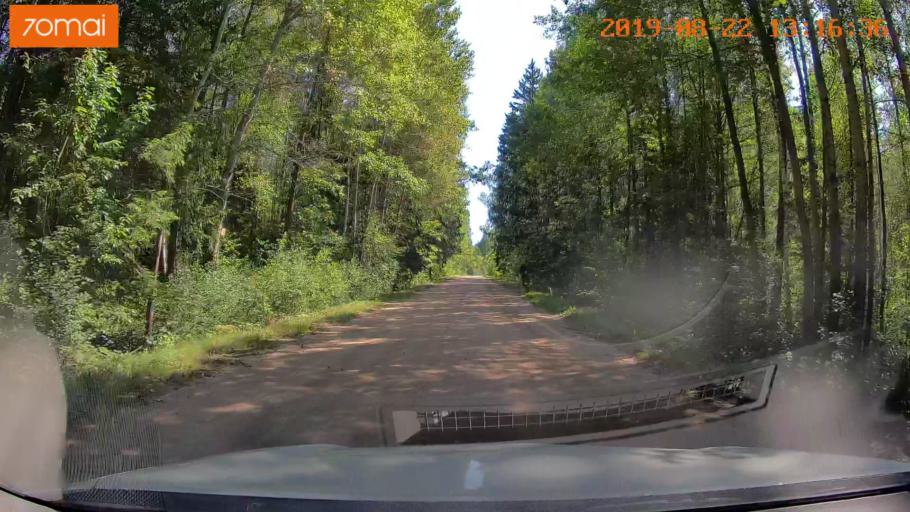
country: BY
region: Minsk
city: Prawdzinski
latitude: 53.2547
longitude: 27.9127
